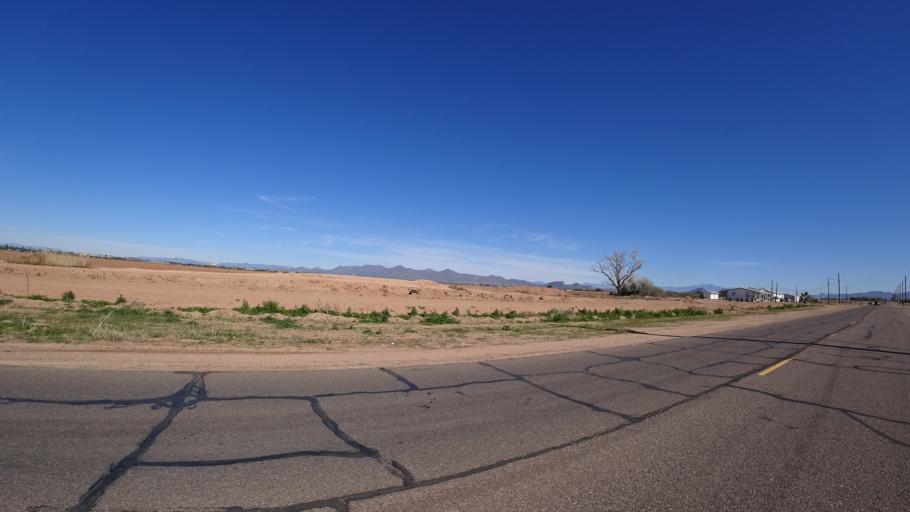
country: US
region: Arizona
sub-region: Maricopa County
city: Scottsdale
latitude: 33.4949
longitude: -111.8842
